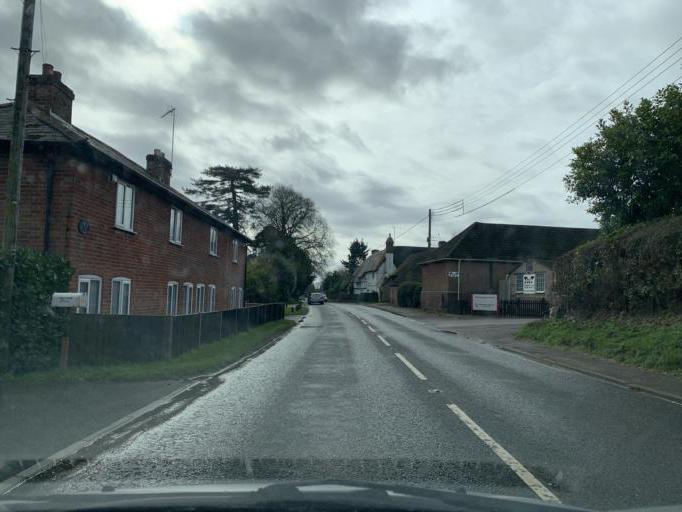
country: GB
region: England
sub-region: Hampshire
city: Fordingbridge
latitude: 50.9415
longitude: -1.7840
